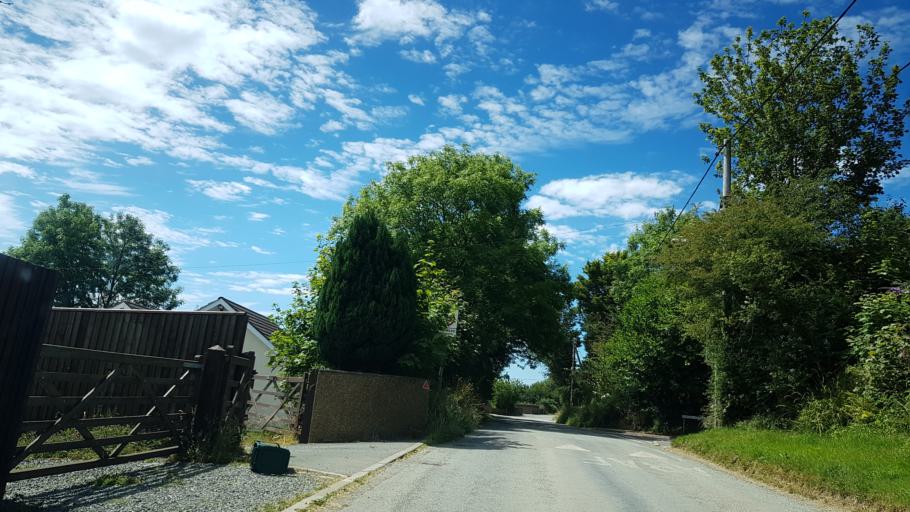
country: GB
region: Wales
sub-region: Pembrokeshire
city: Wiston
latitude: 51.8264
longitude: -4.8741
